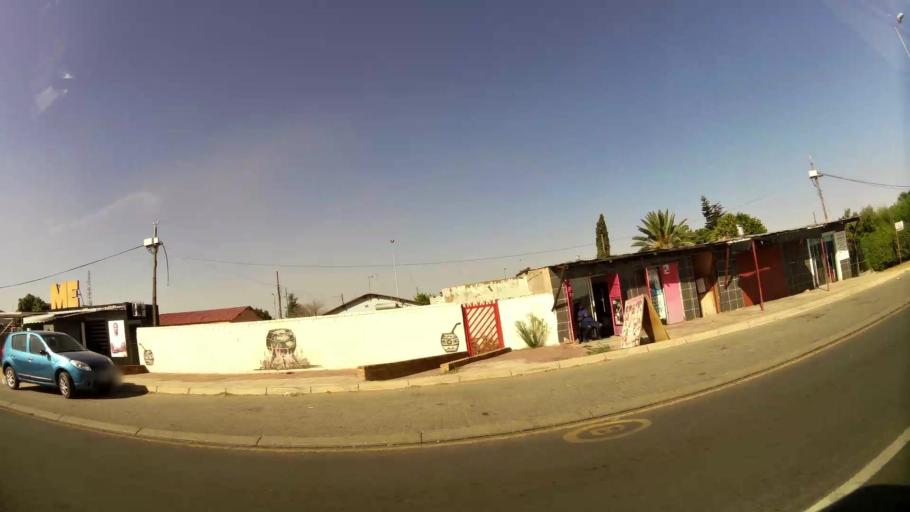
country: ZA
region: Gauteng
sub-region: City of Tshwane Metropolitan Municipality
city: Mabopane
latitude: -25.5394
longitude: 28.0985
